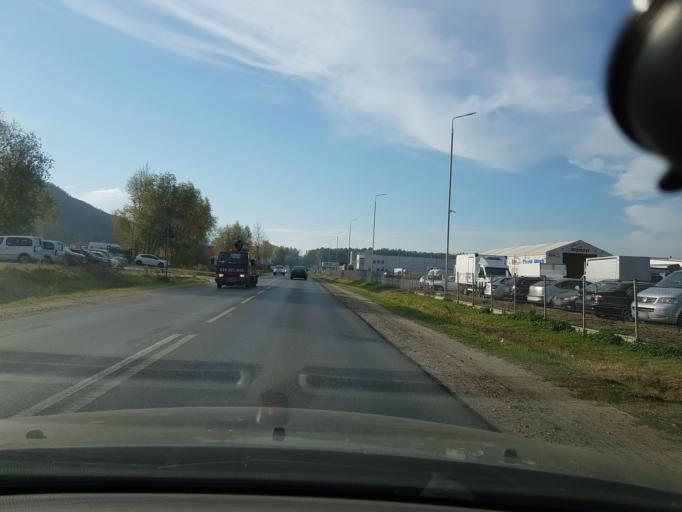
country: PL
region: Masovian Voivodeship
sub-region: Powiat warszawski zachodni
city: Babice
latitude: 52.2793
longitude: 20.8757
